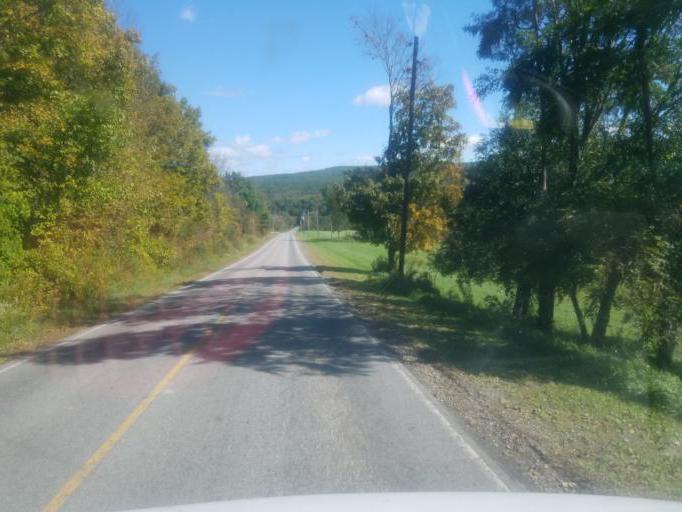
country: US
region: New York
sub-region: Allegany County
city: Friendship
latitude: 42.2766
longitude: -78.1381
